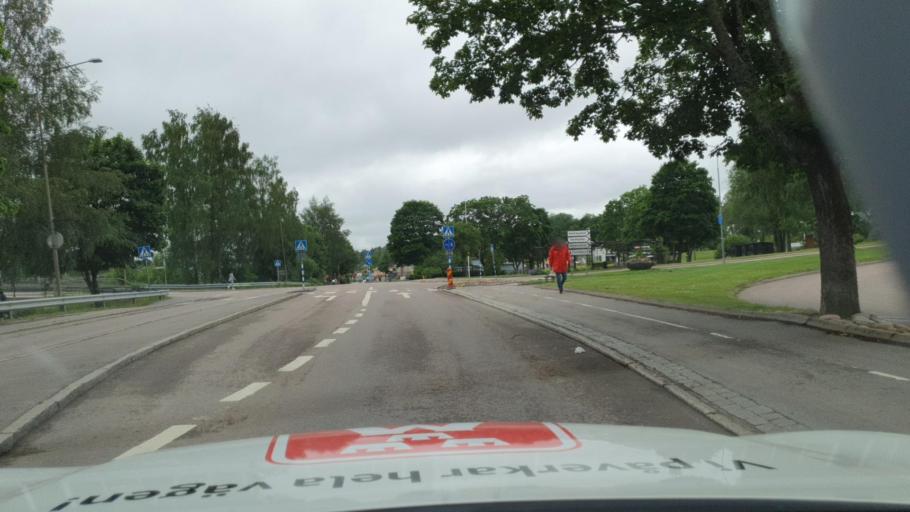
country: SE
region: Vaermland
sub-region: Grums Kommun
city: Grums
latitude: 59.3511
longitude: 13.1116
